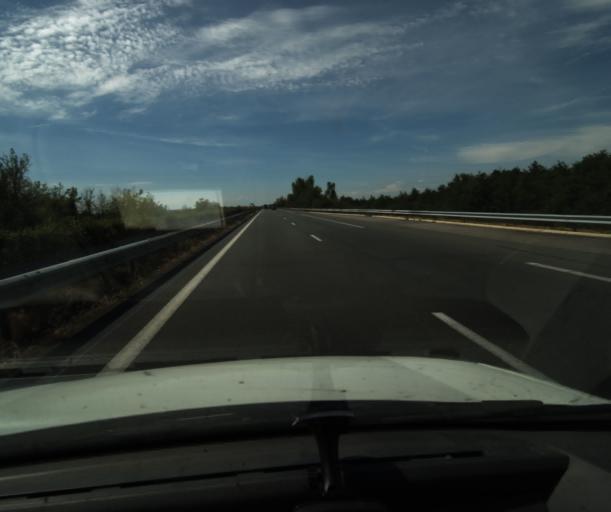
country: FR
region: Midi-Pyrenees
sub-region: Departement du Tarn-et-Garonne
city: Saint-Porquier
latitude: 44.0336
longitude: 1.1588
